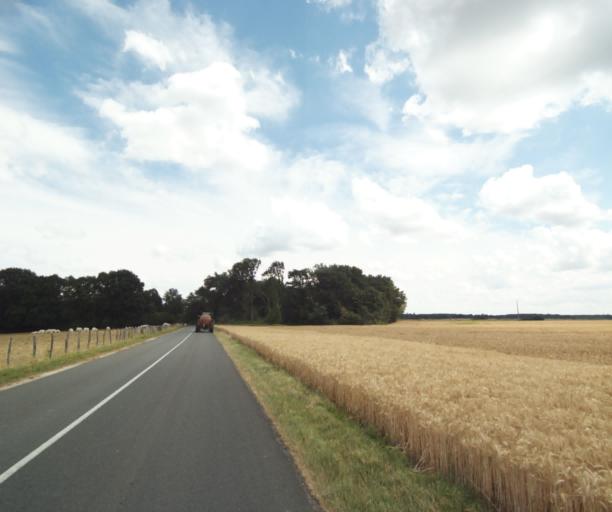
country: FR
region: Ile-de-France
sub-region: Departement de Seine-et-Marne
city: Hericy
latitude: 48.4425
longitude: 2.7888
